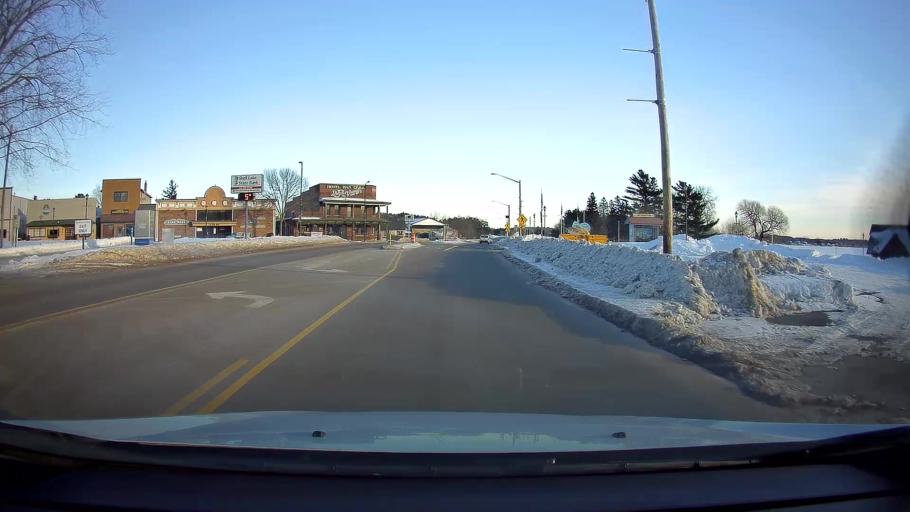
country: US
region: Wisconsin
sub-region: Washburn County
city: Shell Lake
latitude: 45.7425
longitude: -91.9240
